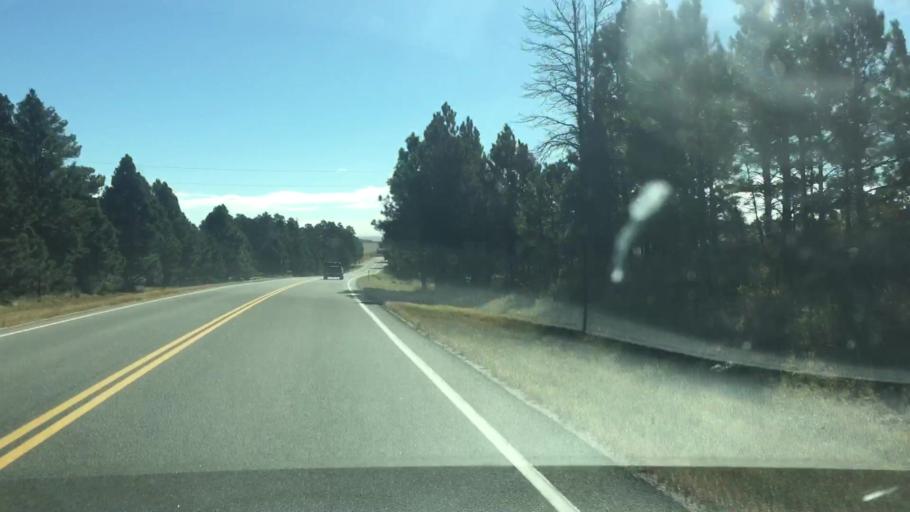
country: US
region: Colorado
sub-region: Elbert County
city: Kiowa
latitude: 39.3315
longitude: -104.4119
